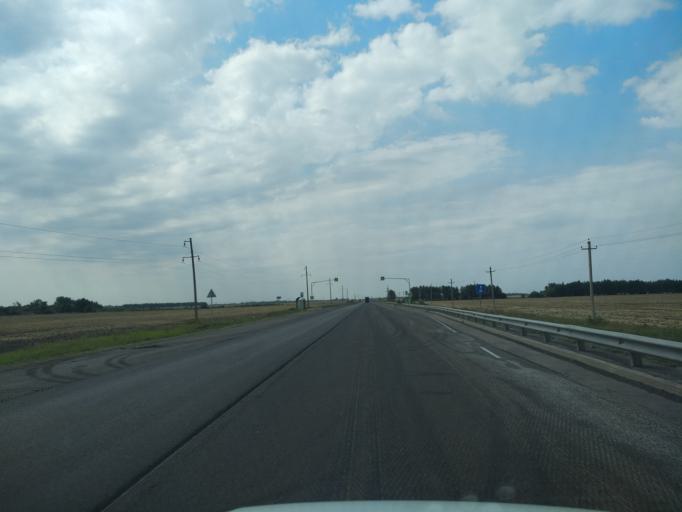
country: RU
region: Voronezj
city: Pereleshino
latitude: 51.7979
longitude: 40.1511
